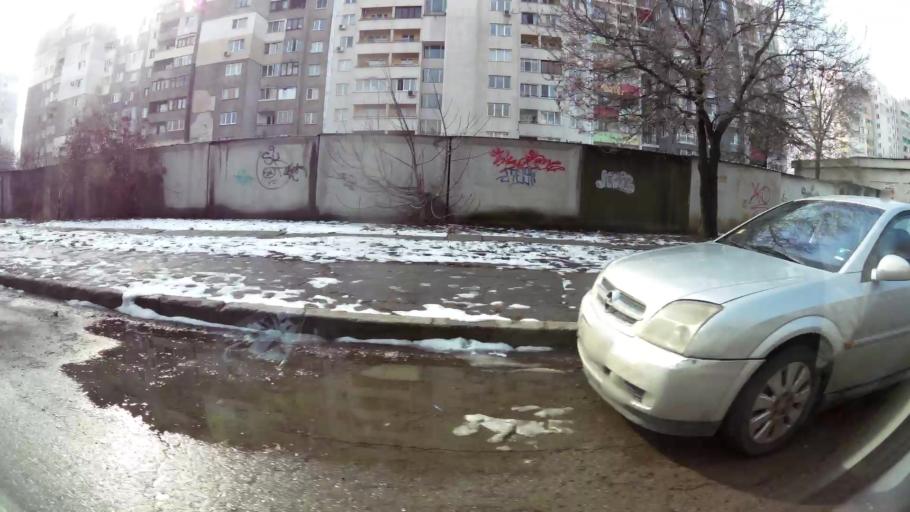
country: BG
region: Sofia-Capital
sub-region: Stolichna Obshtina
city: Sofia
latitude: 42.7165
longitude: 23.2638
